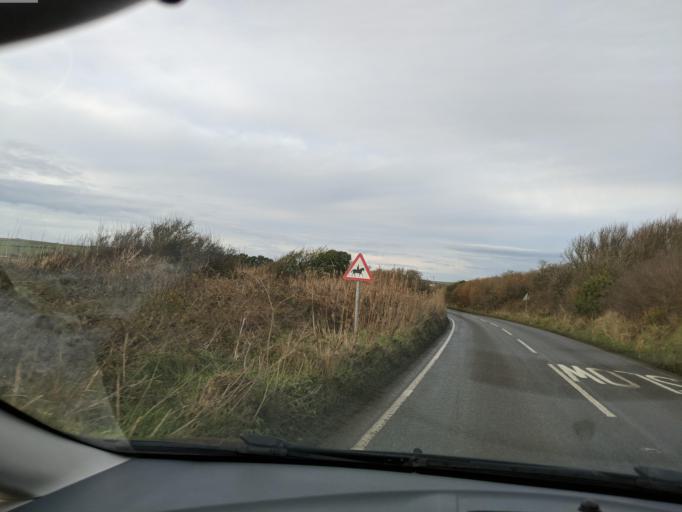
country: GB
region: England
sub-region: Cornwall
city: Jacobstow
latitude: 50.6921
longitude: -4.6160
